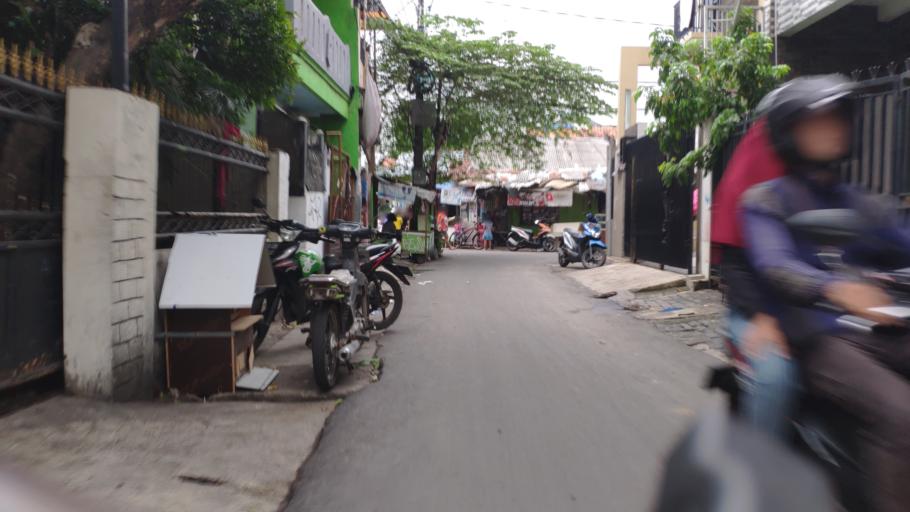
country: ID
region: Jakarta Raya
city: Jakarta
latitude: -6.2111
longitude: 106.8398
